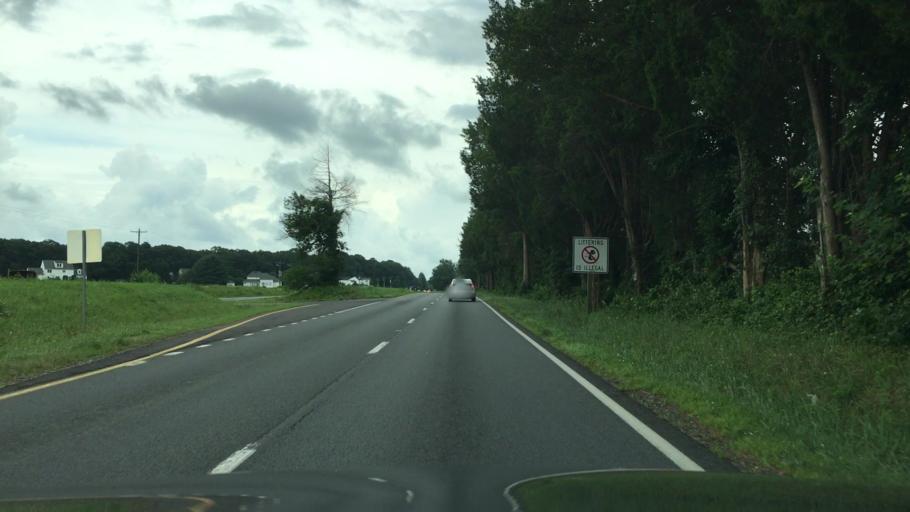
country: US
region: Virginia
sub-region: Spotsylvania County
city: Spotsylvania
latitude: 38.3243
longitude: -77.7201
